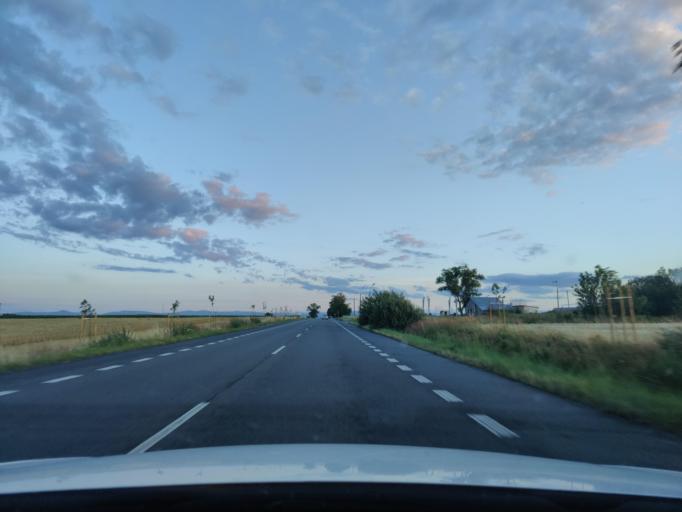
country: PL
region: Opole Voivodeship
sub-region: Powiat nyski
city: Pakoslawice
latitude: 50.5536
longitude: 17.3770
